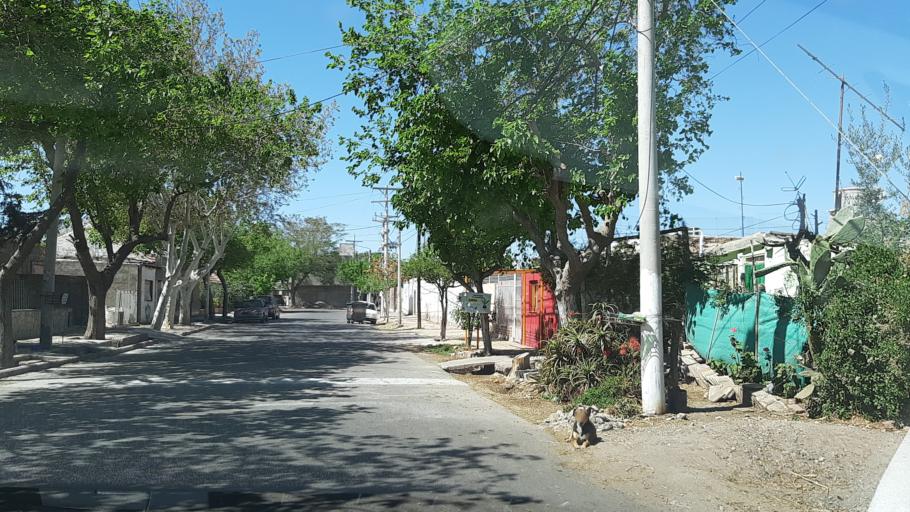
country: AR
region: San Juan
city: San Juan
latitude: -31.5287
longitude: -68.5488
